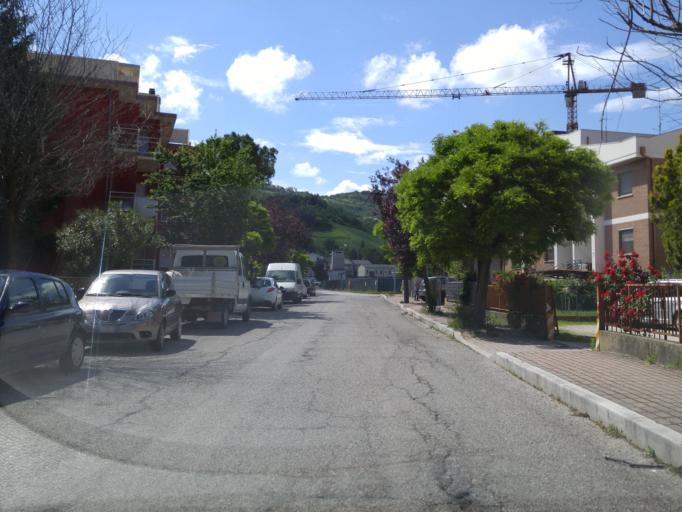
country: IT
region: The Marches
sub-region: Provincia di Pesaro e Urbino
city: Fermignano
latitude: 43.6827
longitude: 12.6461
